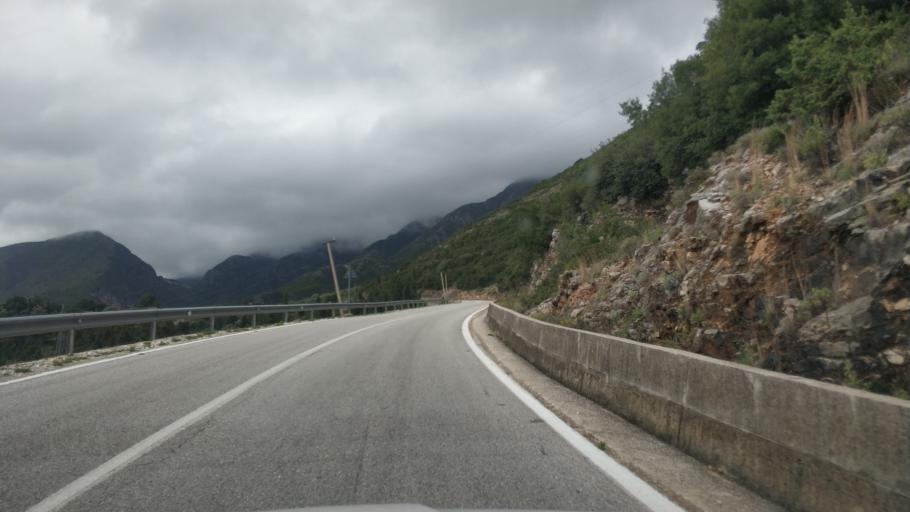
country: AL
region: Vlore
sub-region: Rrethi i Vlores
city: Vranisht
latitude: 40.1427
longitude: 19.6869
